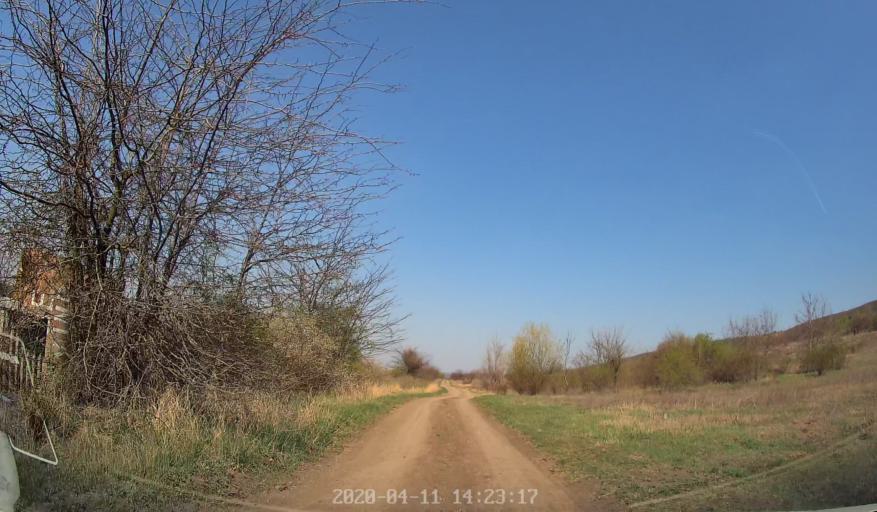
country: MD
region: Chisinau
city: Vadul lui Voda
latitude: 47.0902
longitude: 29.1394
